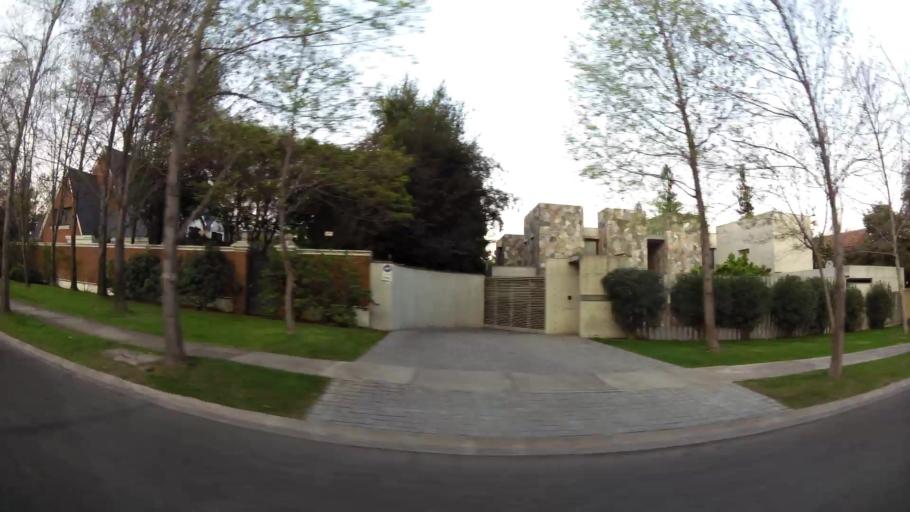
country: CL
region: Santiago Metropolitan
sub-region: Provincia de Chacabuco
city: Chicureo Abajo
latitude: -33.3412
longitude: -70.5538
